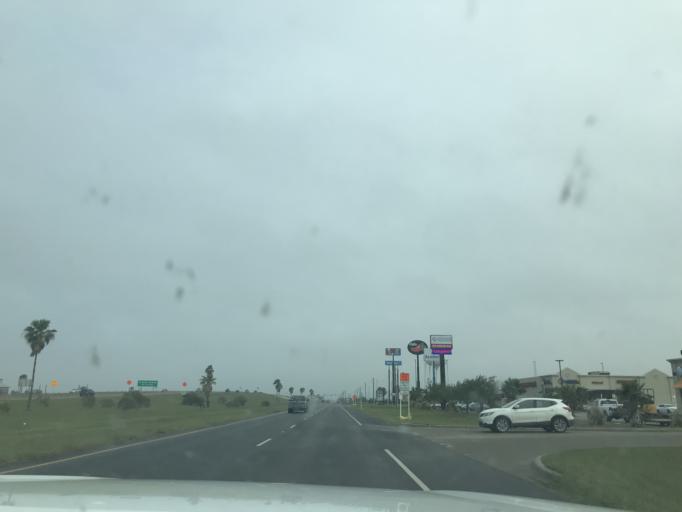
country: US
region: Texas
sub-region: San Patricio County
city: Portland
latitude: 27.8934
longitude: -97.3094
